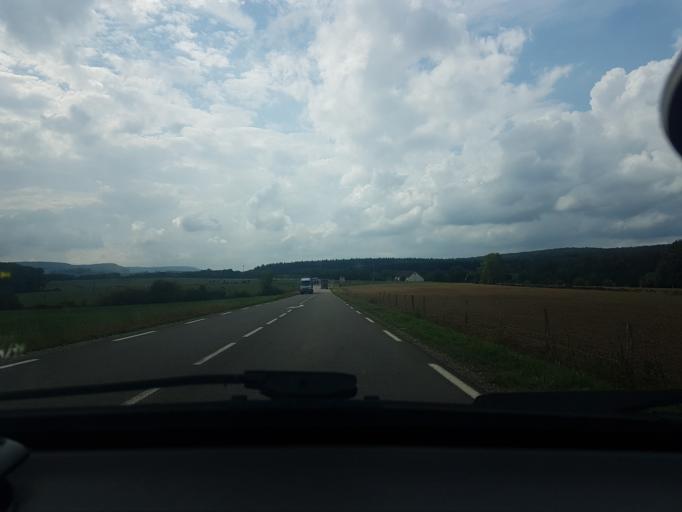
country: FR
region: Franche-Comte
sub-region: Departement du Doubs
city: Arcey
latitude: 47.5794
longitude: 6.6642
